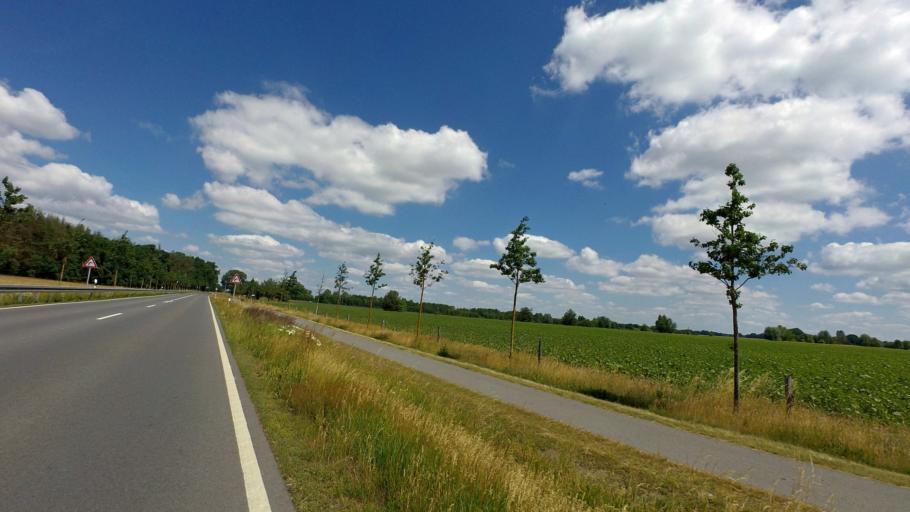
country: DE
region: Brandenburg
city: Sonnewalde
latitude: 51.6707
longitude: 13.6421
